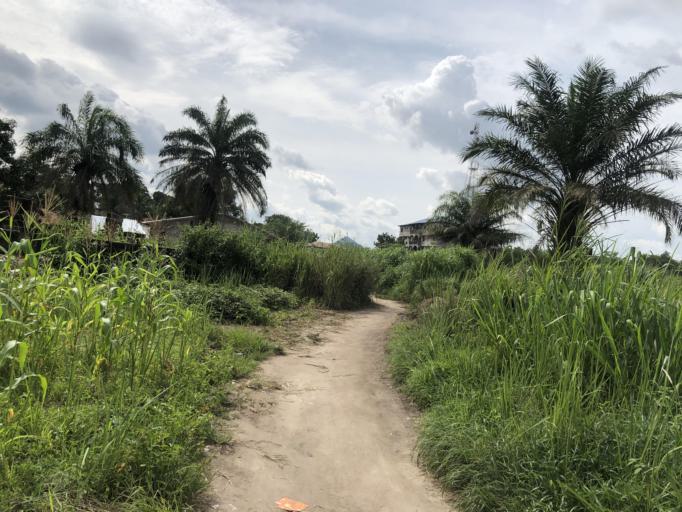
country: SL
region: Northern Province
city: Magburaka
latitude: 8.7181
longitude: -11.9327
